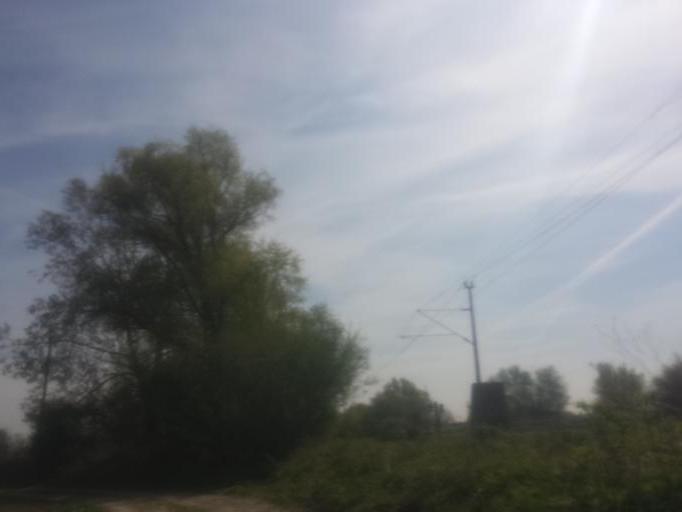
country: DE
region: Bavaria
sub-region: Upper Bavaria
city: Manching
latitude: 48.7282
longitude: 11.4697
